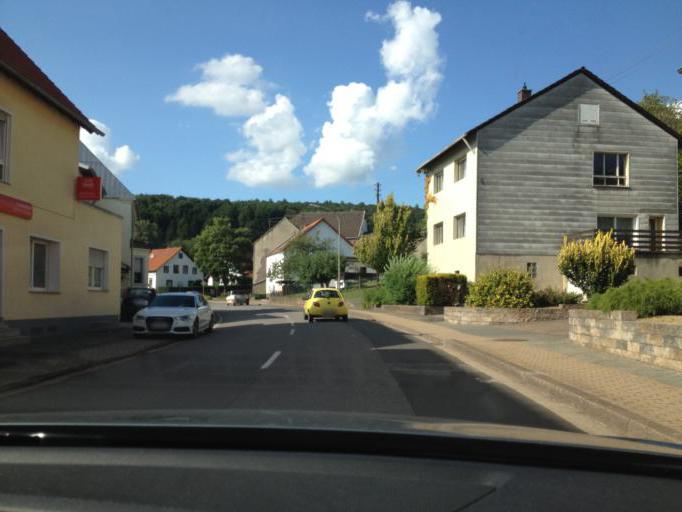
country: DE
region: Saarland
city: Illingen
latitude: 49.4005
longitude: 7.0352
